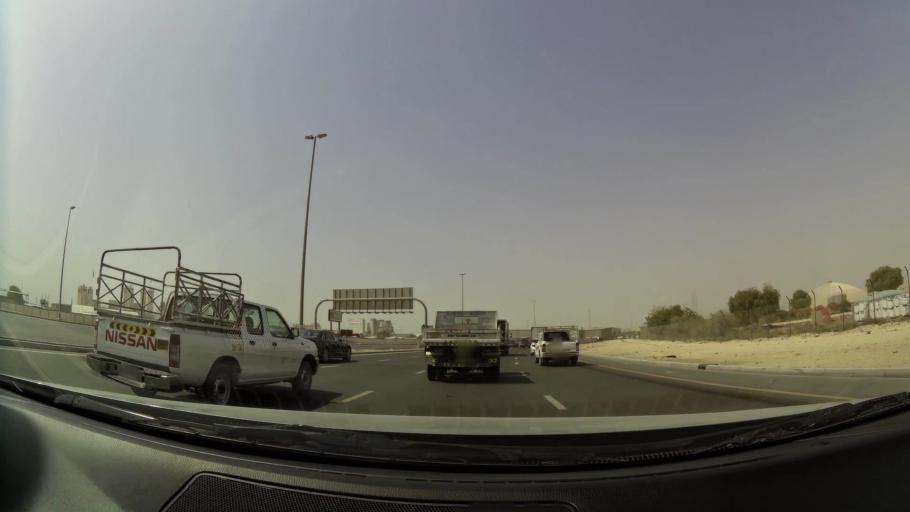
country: AE
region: Dubai
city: Dubai
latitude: 25.1562
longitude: 55.2366
